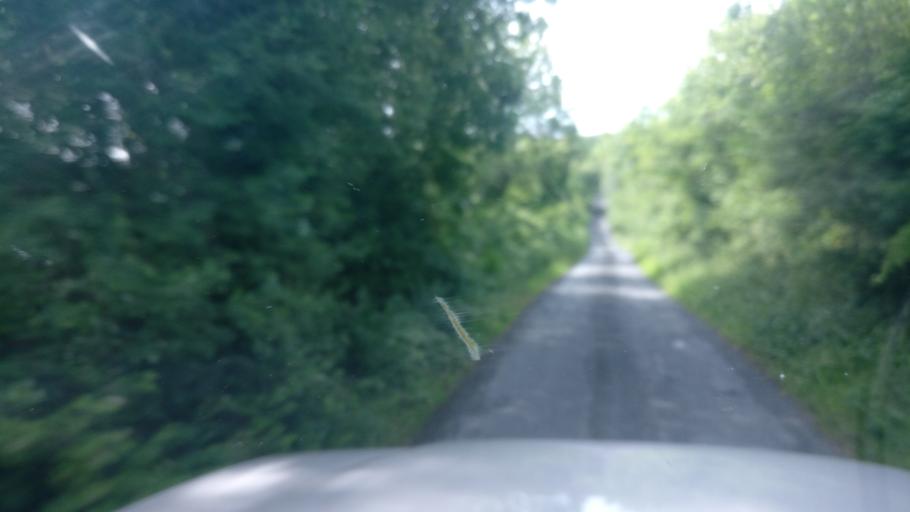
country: IE
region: Connaught
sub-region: County Galway
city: Gort
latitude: 53.0990
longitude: -8.6991
